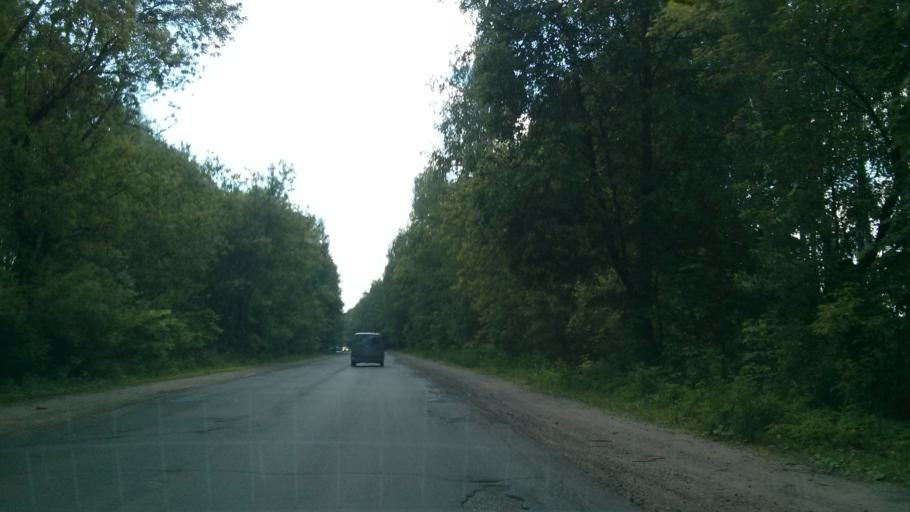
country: RU
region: Vladimir
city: Murom
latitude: 55.5429
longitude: 41.9852
